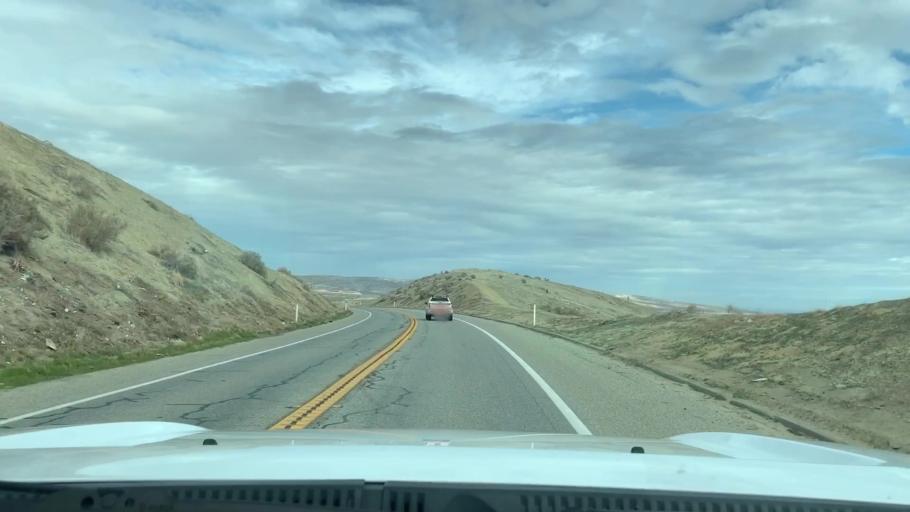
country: US
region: California
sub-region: Kern County
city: Maricopa
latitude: 35.0792
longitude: -119.4009
